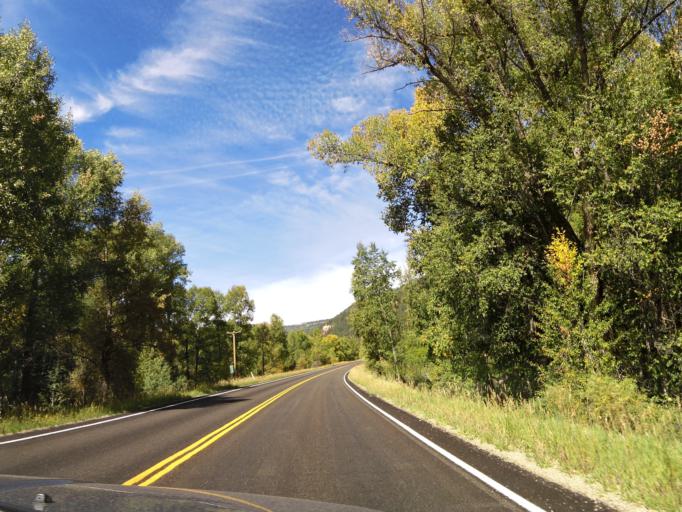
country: US
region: Colorado
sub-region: Montezuma County
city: Mancos
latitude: 37.5766
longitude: -108.2029
